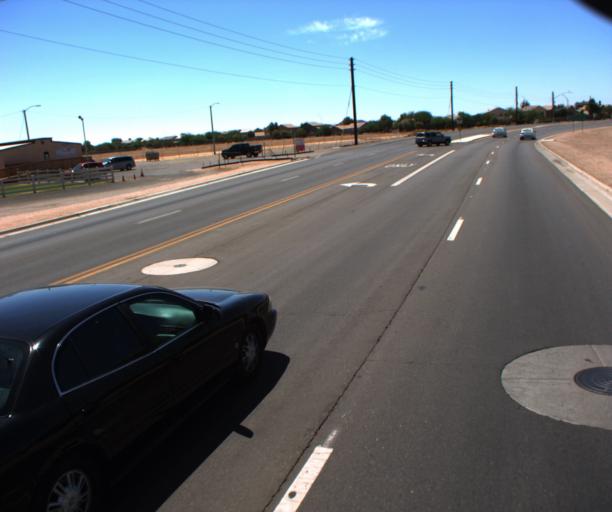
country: US
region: Arizona
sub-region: Pinal County
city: Maricopa
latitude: 33.0498
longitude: -112.0488
